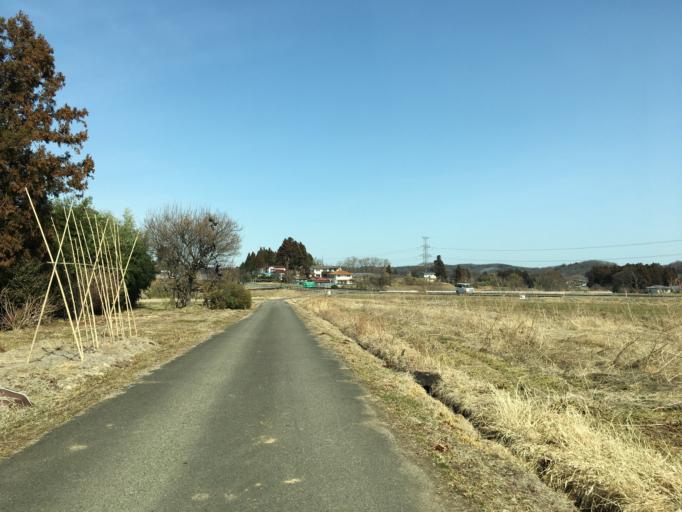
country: JP
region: Fukushima
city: Motomiya
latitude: 37.5587
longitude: 140.3833
